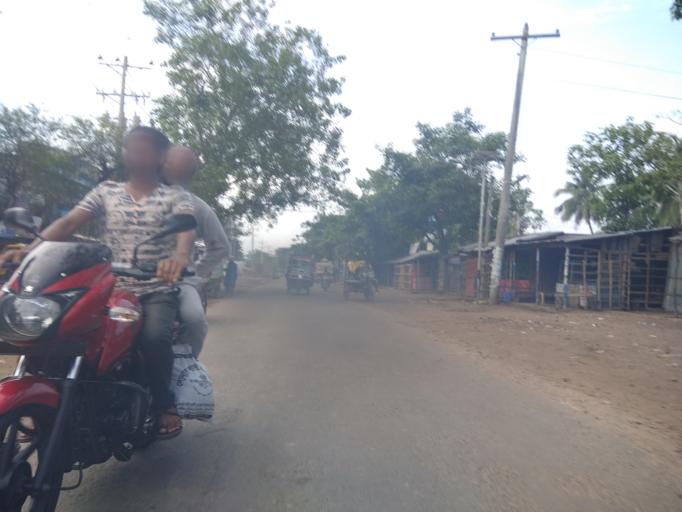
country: IN
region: West Bengal
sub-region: North 24 Parganas
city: Taki
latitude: 22.3430
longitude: 89.1050
